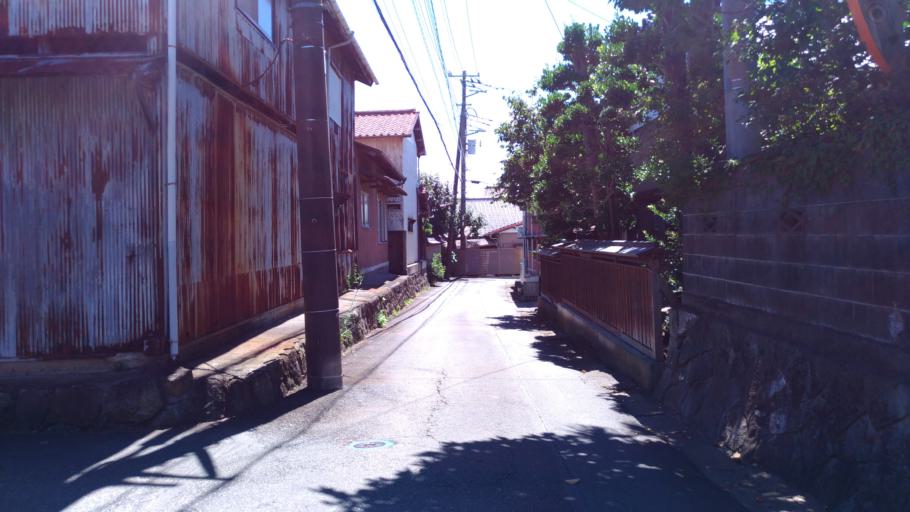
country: JP
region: Shizuoka
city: Mishima
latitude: 35.0850
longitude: 138.9558
